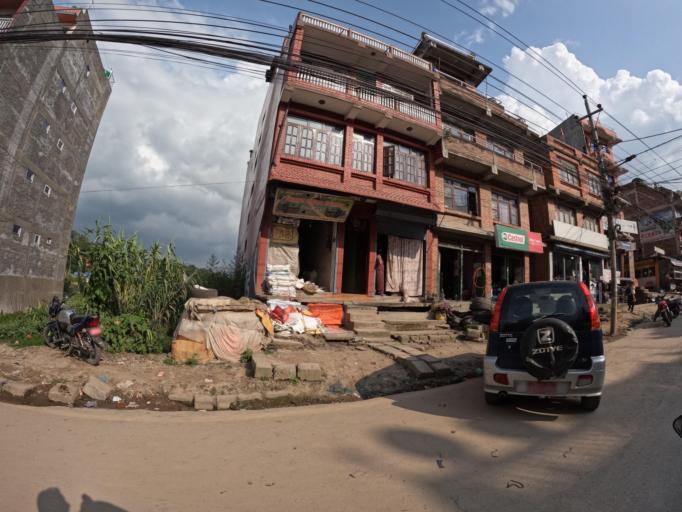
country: NP
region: Central Region
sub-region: Bagmati Zone
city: Bhaktapur
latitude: 27.6686
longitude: 85.4373
